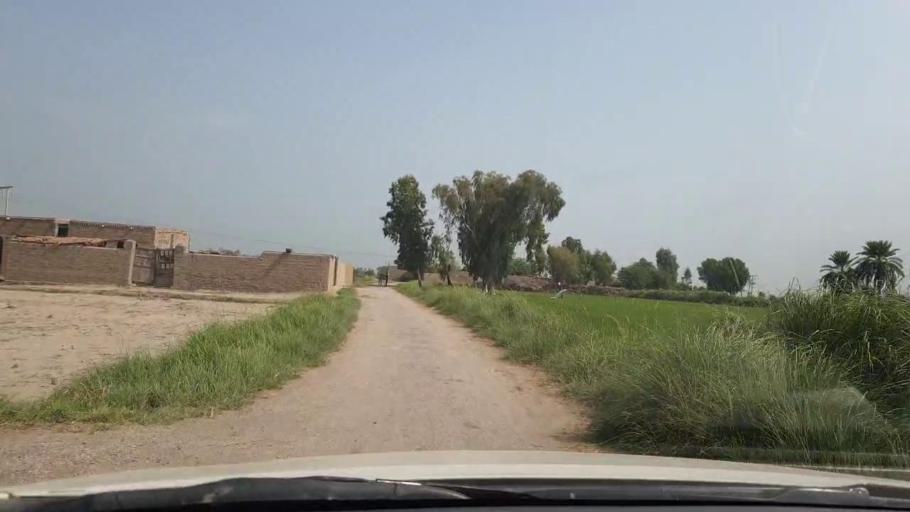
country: PK
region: Sindh
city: Shikarpur
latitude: 27.9736
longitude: 68.6704
